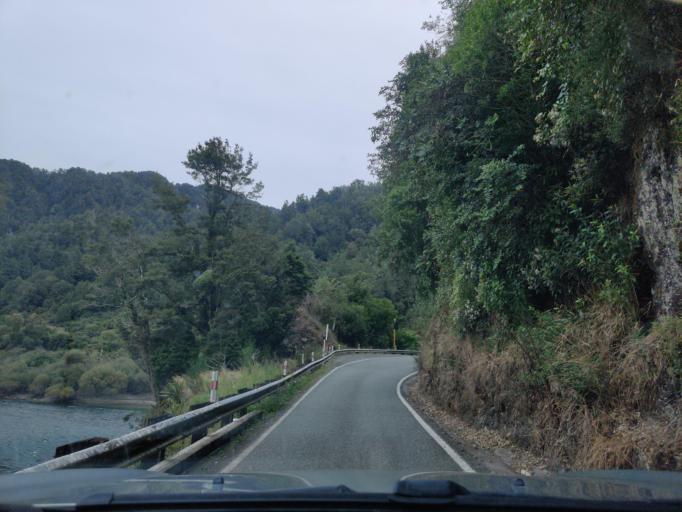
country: NZ
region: West Coast
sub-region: Buller District
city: Westport
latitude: -41.8485
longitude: 171.7428
